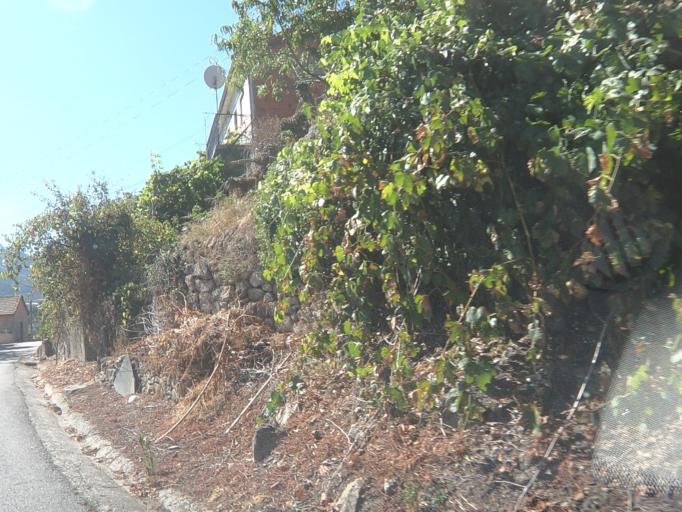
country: PT
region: Vila Real
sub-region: Santa Marta de Penaguiao
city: Santa Marta de Penaguiao
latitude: 41.2529
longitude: -7.8096
